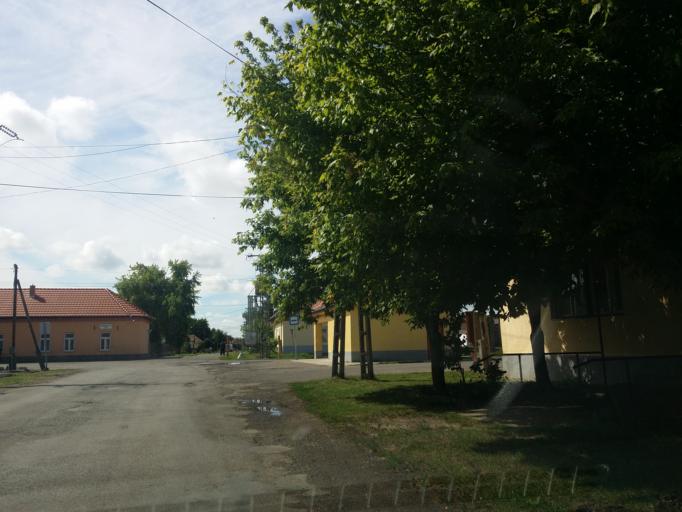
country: HU
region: Heves
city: Heves
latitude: 47.6153
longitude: 20.3594
